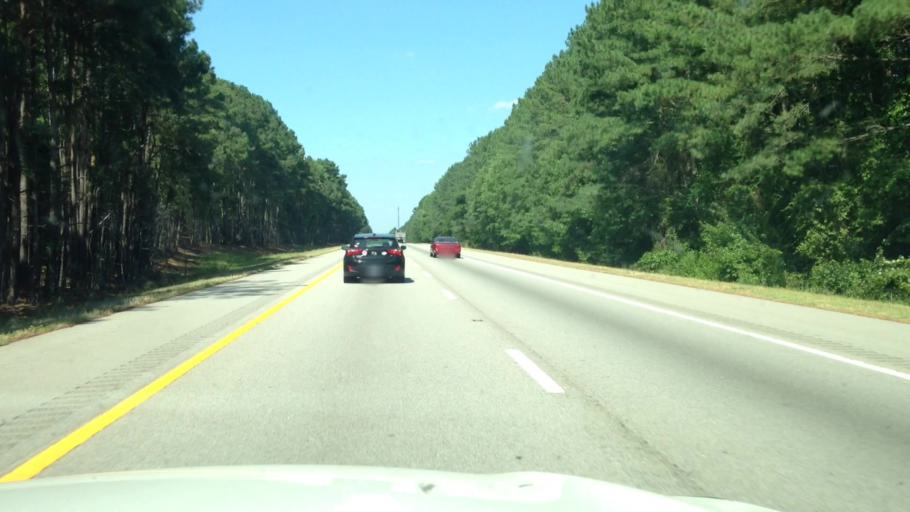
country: US
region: North Carolina
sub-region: Wilson County
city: Lucama
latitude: 35.6662
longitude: -78.0832
